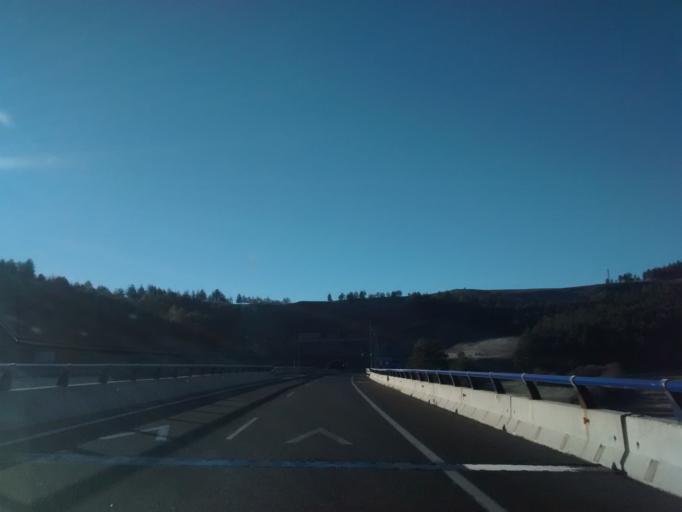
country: ES
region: Castille and Leon
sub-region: Provincia de Palencia
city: Alar del Rey
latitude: 42.6886
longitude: -4.2992
